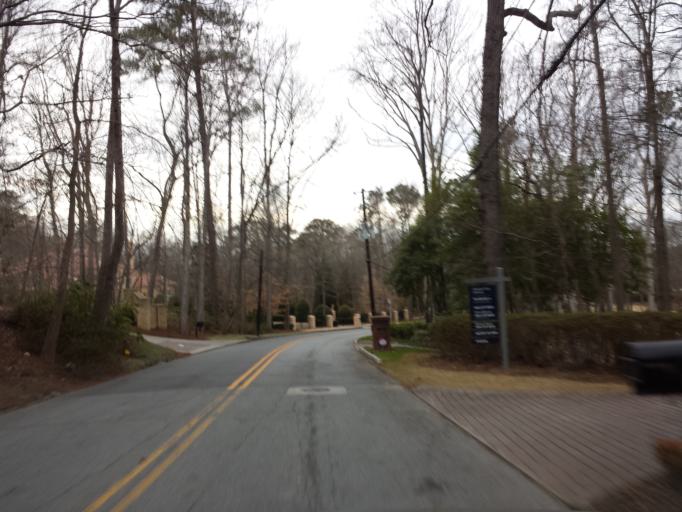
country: US
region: Georgia
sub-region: Cobb County
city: Vinings
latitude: 33.8689
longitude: -84.4332
